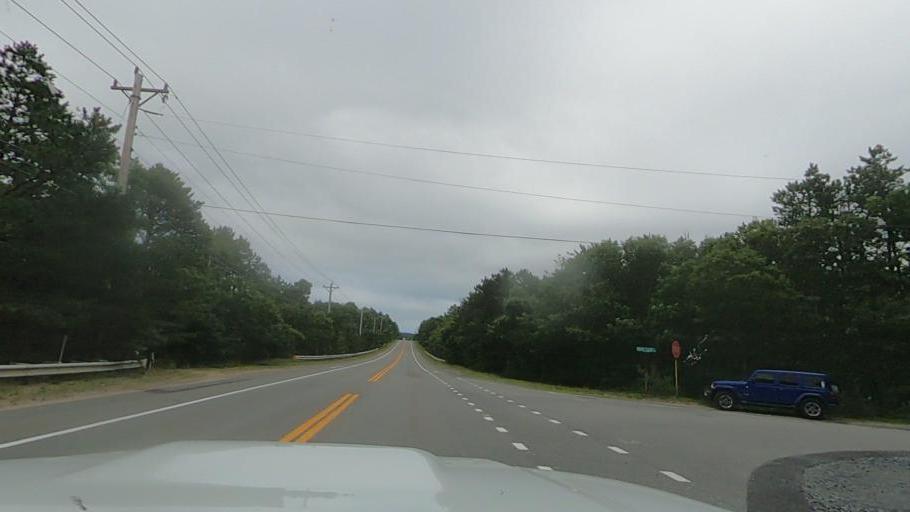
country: US
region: Massachusetts
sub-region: Barnstable County
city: Truro
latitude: 41.9785
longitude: -70.0405
